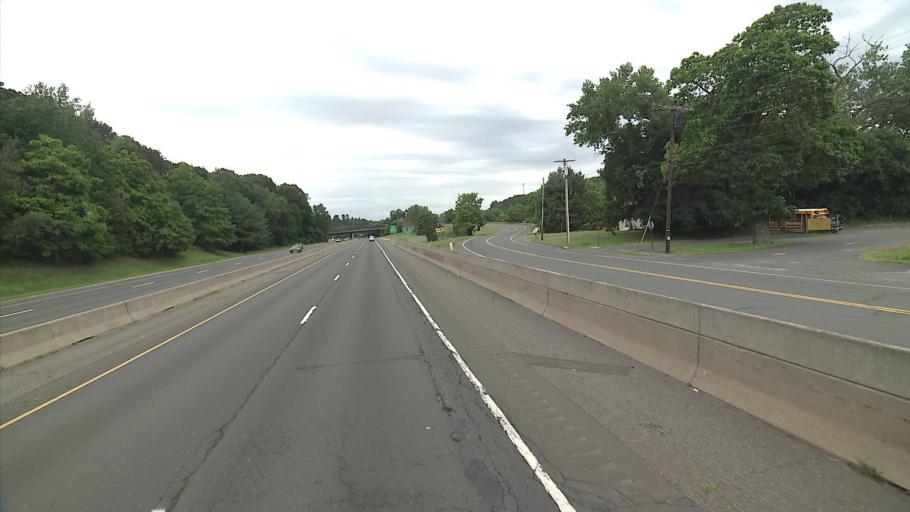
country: US
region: Connecticut
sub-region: New Haven County
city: Seymour
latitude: 41.4099
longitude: -73.0702
